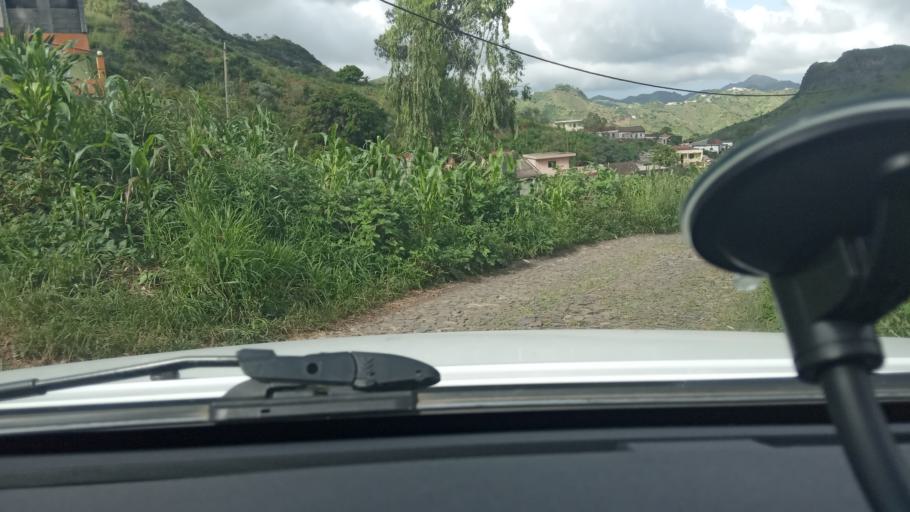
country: CV
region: Sao Salvador do Mundo
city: Picos
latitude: 15.0951
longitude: -23.6509
